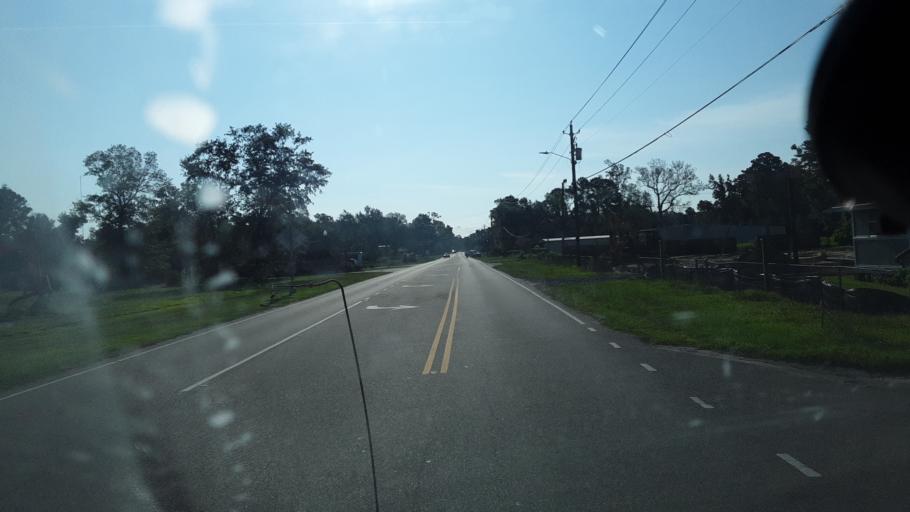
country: US
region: North Carolina
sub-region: Brunswick County
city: Leland
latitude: 34.2480
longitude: -78.0276
